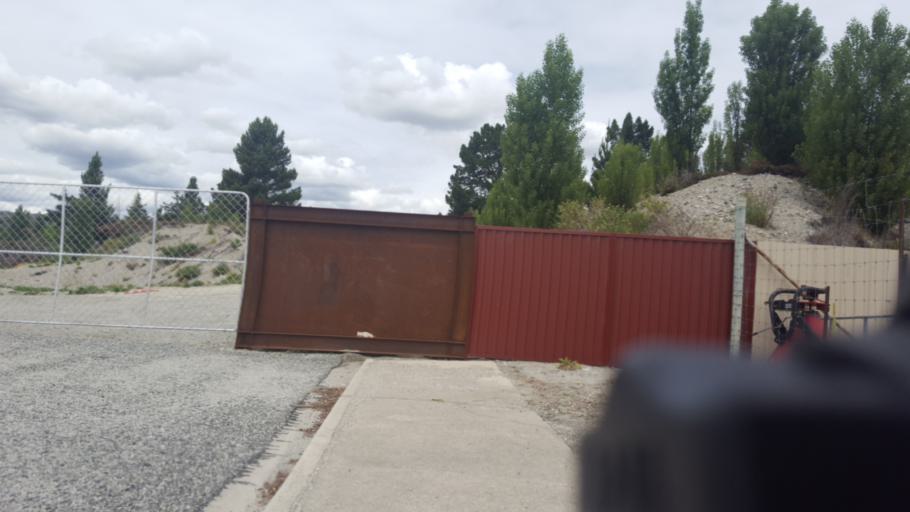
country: NZ
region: Otago
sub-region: Queenstown-Lakes District
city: Wanaka
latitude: -45.2492
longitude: 169.3744
